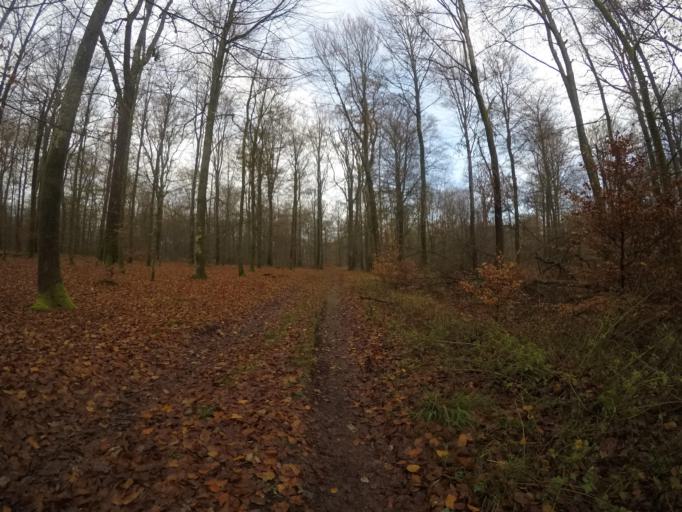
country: BE
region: Wallonia
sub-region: Province du Luxembourg
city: Habay-la-Vieille
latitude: 49.7455
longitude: 5.5931
